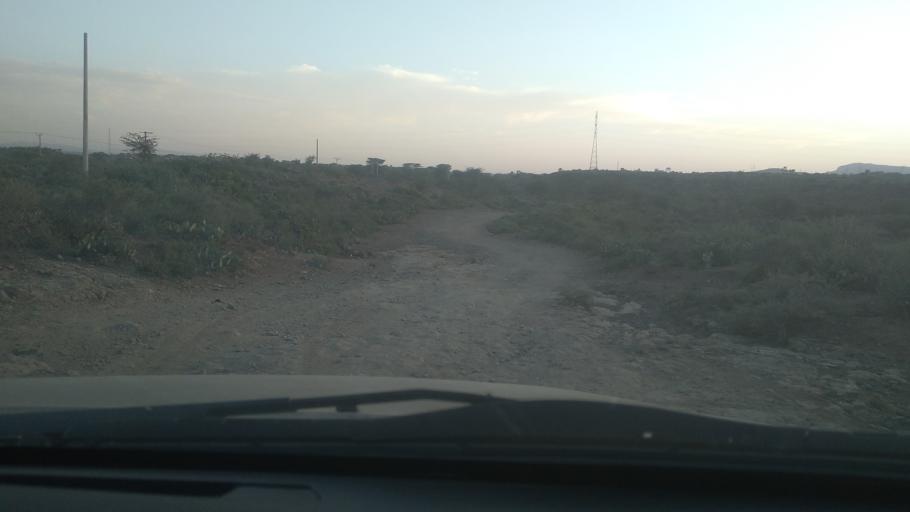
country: ET
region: Oromiya
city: Asbe Teferi
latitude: 9.2422
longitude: 40.7692
